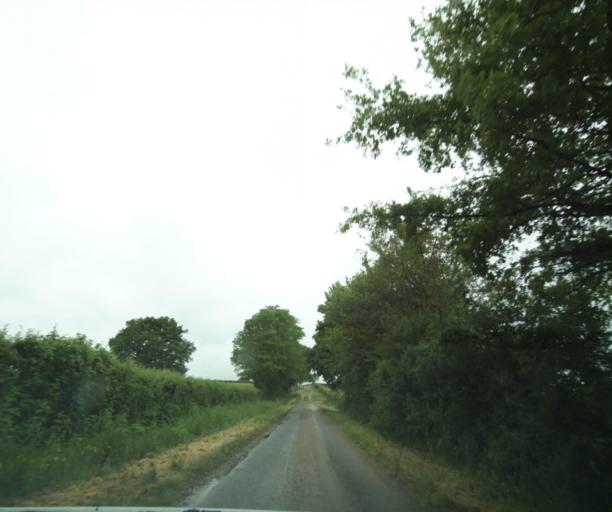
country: FR
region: Bourgogne
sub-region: Departement de Saone-et-Loire
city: Palinges
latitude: 46.5678
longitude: 4.2071
